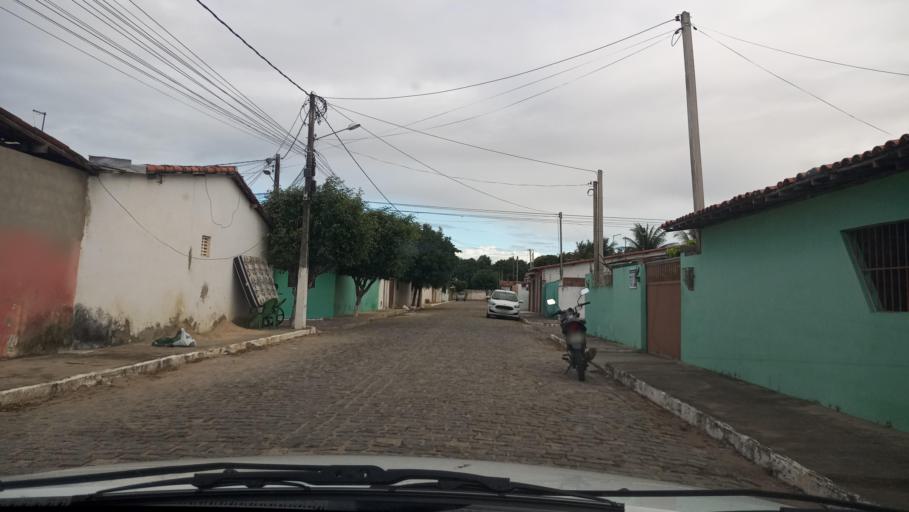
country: BR
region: Rio Grande do Norte
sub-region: Brejinho
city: Brejinho
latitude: -6.0491
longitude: -35.4335
